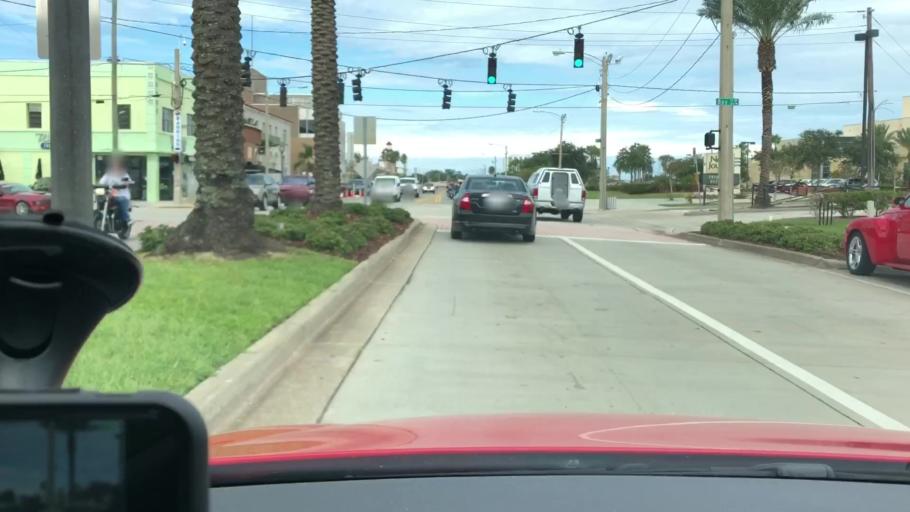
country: US
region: Florida
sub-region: Volusia County
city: Daytona Beach
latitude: 29.2139
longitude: -81.0201
